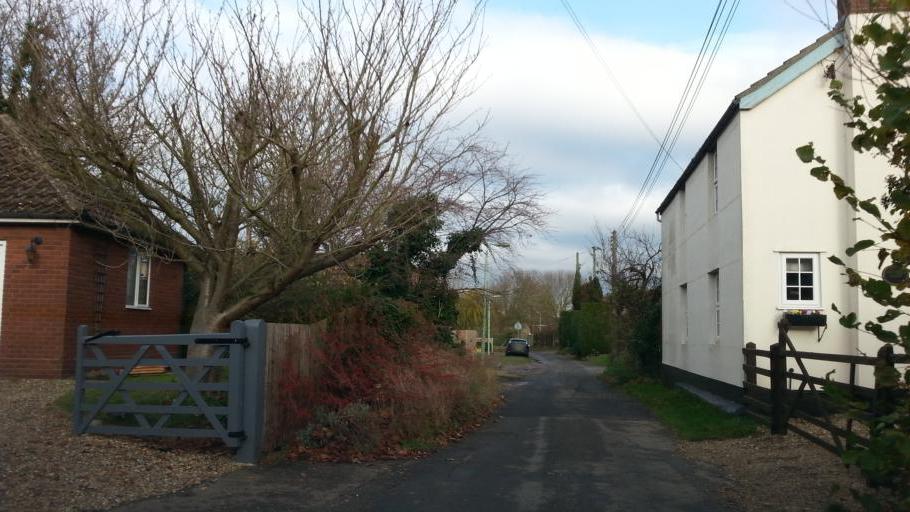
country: GB
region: England
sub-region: Suffolk
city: Ixworth
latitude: 52.3242
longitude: 0.8845
